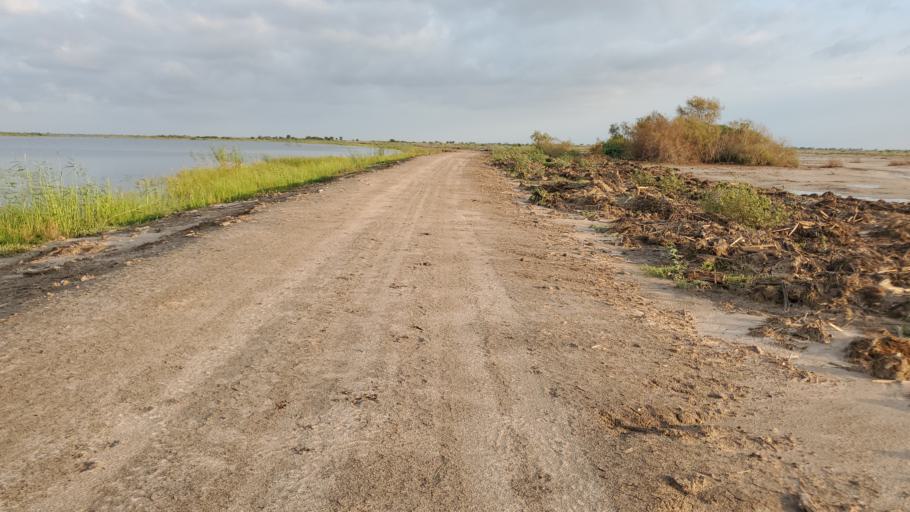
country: SN
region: Saint-Louis
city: Saint-Louis
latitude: 16.0245
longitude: -16.4099
